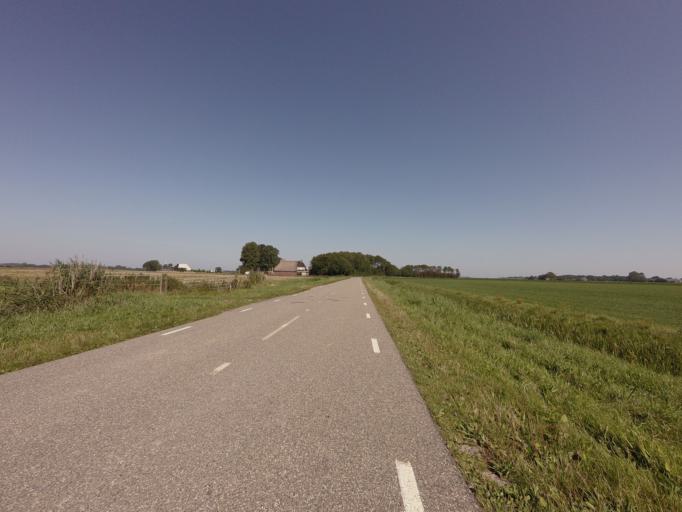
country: NL
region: Friesland
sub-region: Gemeente Dongeradeel
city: Ternaard
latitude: 53.3650
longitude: 5.9813
